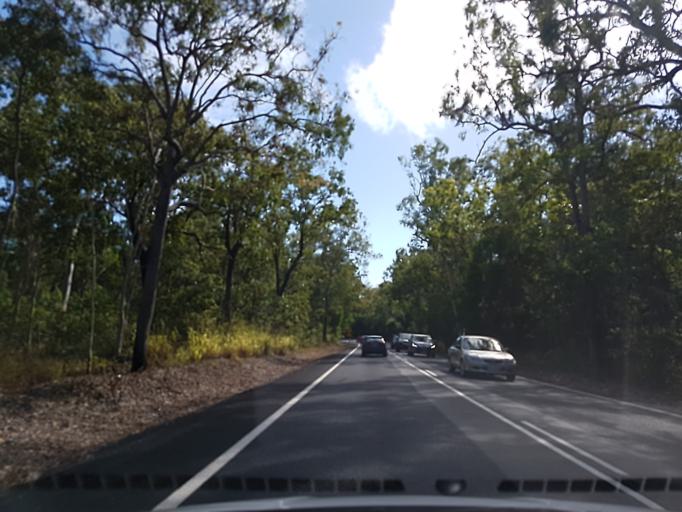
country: AU
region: Queensland
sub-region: Cairns
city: Palm Cove
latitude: -16.6689
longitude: 145.5680
